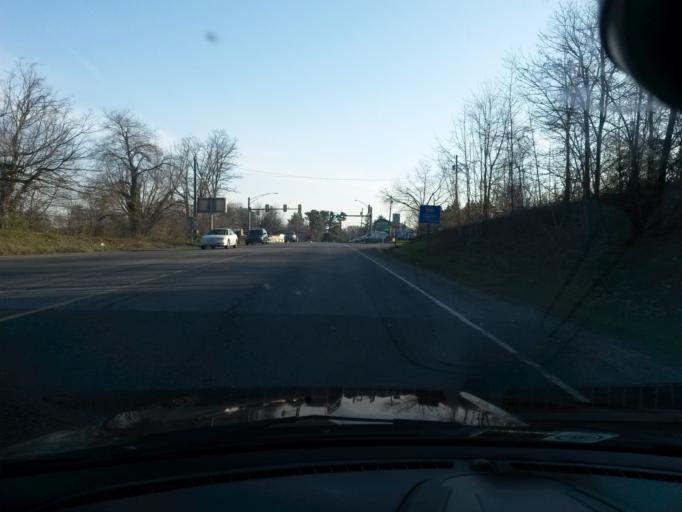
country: US
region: Virginia
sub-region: Montgomery County
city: Christiansburg
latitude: 37.1175
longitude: -80.4218
